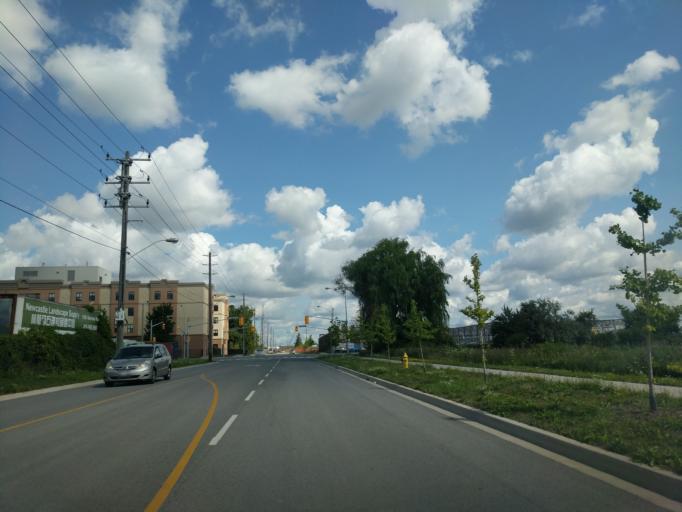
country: CA
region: Ontario
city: Scarborough
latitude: 43.8120
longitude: -79.2989
